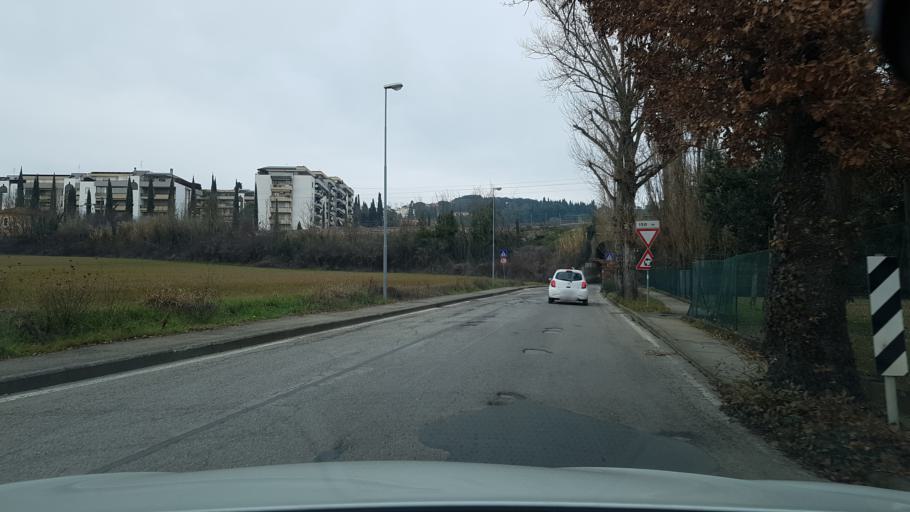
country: IT
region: Umbria
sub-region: Provincia di Perugia
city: Perugia
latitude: 43.1125
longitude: 12.3633
